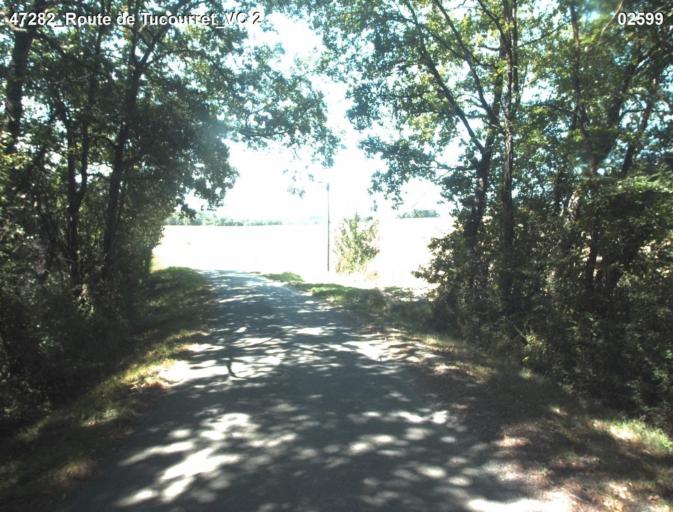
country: FR
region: Aquitaine
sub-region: Departement du Lot-et-Garonne
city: Laplume
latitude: 44.1059
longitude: 0.4977
